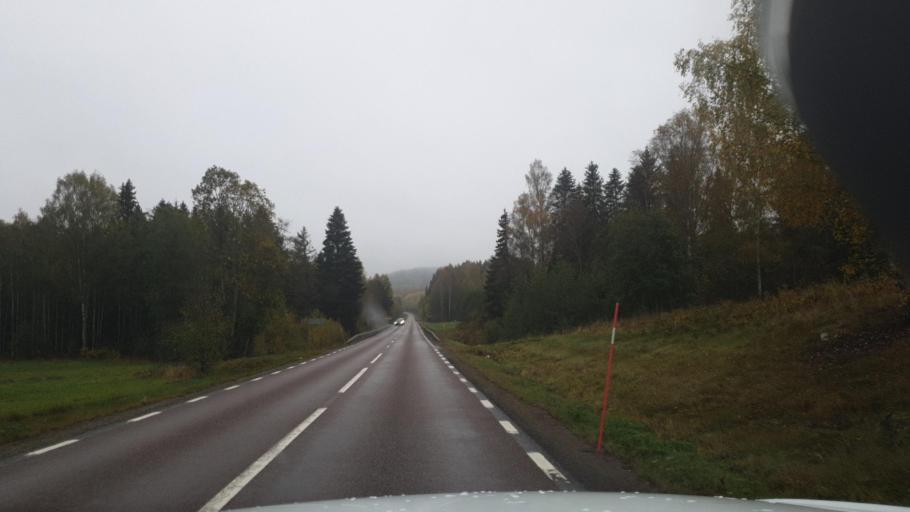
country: SE
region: Vaermland
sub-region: Eda Kommun
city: Amotfors
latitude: 59.7231
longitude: 12.2814
